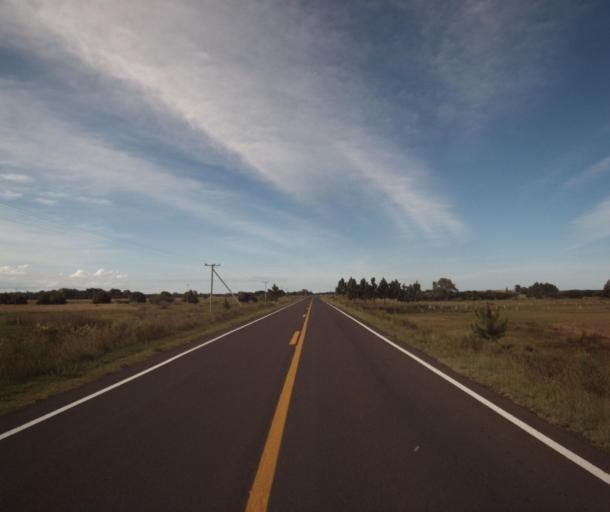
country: BR
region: Rio Grande do Sul
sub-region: Tapes
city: Tapes
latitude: -31.3181
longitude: -51.1212
